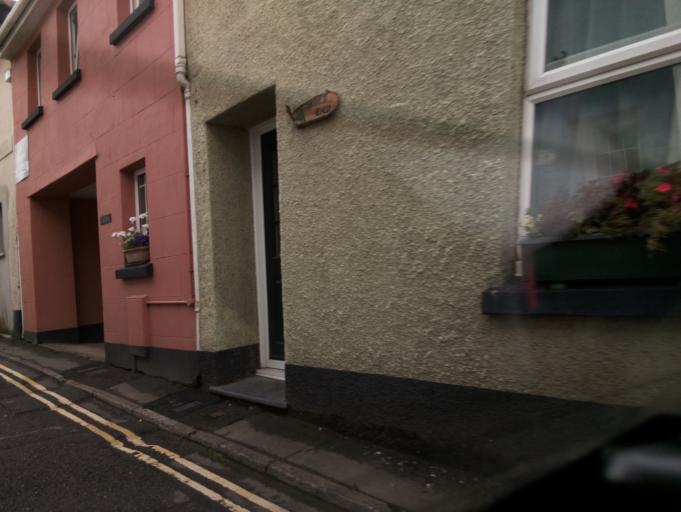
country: GB
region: England
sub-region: Devon
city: Modbury
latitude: 50.3137
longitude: -3.8360
